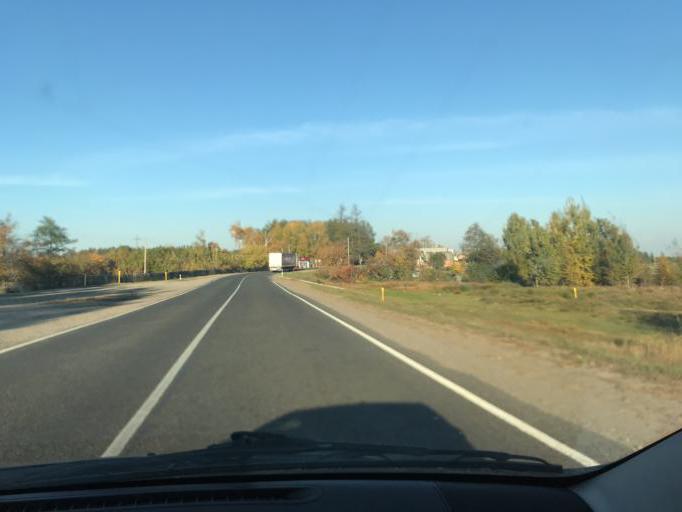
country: BY
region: Brest
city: Stolin
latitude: 51.8302
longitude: 26.7146
